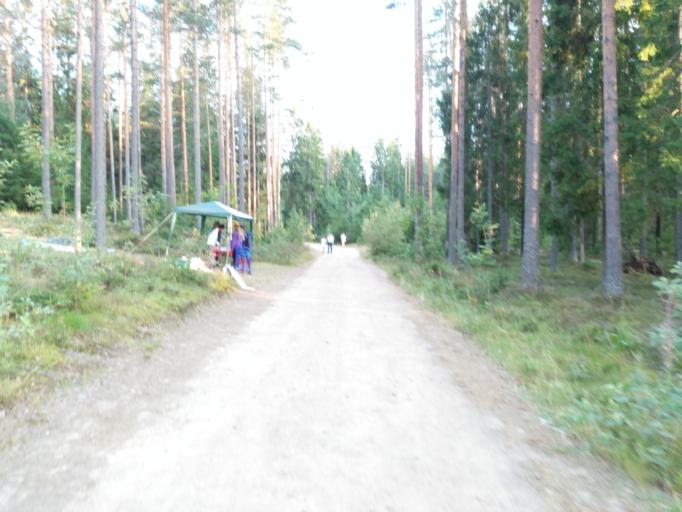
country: RU
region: Leningrad
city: Il'ichevo
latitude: 60.2846
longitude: 29.7437
